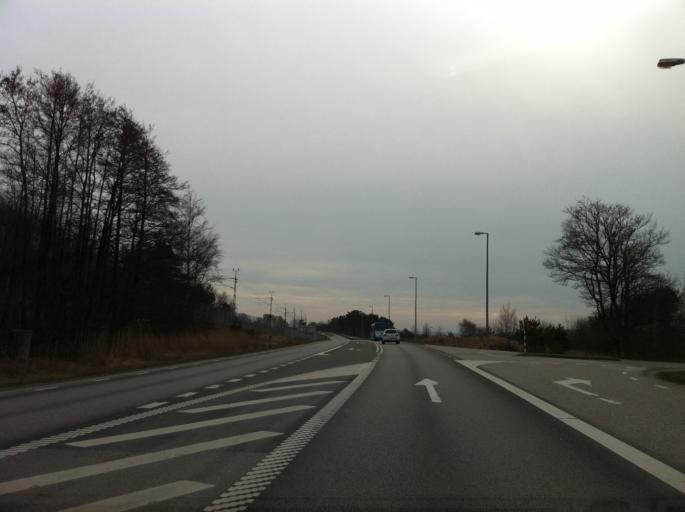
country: SE
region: Vaestra Goetaland
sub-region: Stenungsunds Kommun
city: Stenungsund
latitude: 58.0650
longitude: 11.8081
